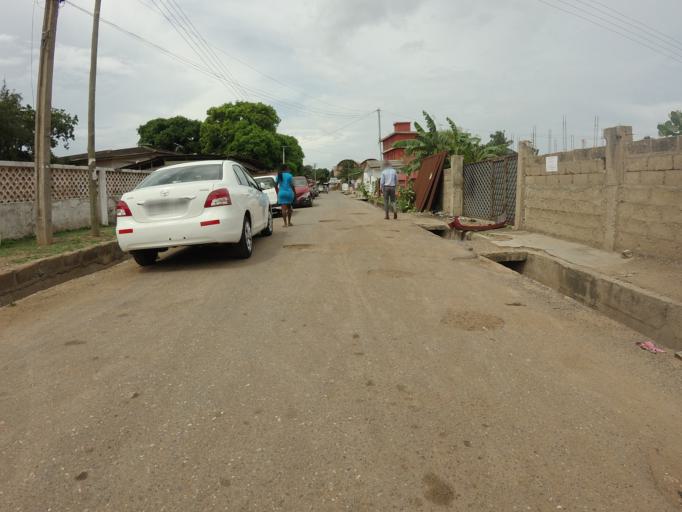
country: GH
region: Greater Accra
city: Accra
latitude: 5.5952
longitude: -0.2190
